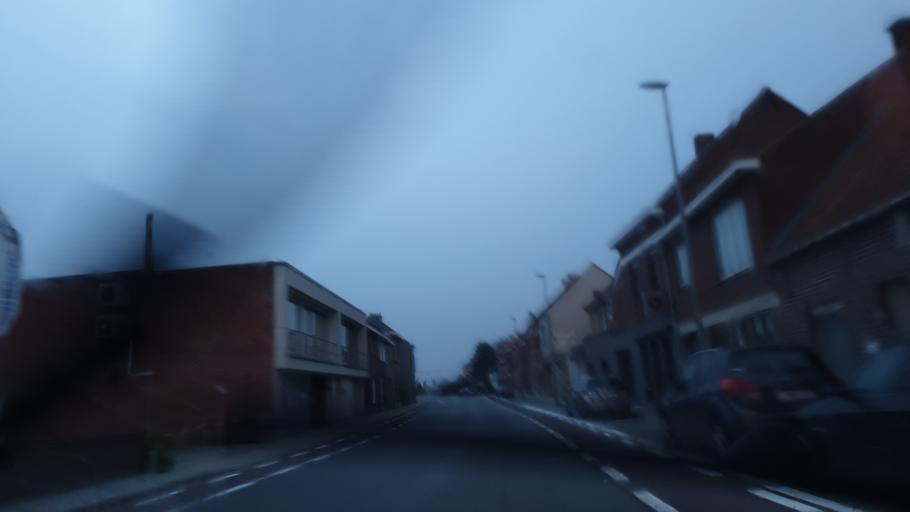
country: BE
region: Flanders
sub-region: Provincie West-Vlaanderen
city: Ieper
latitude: 50.8670
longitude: 2.8514
